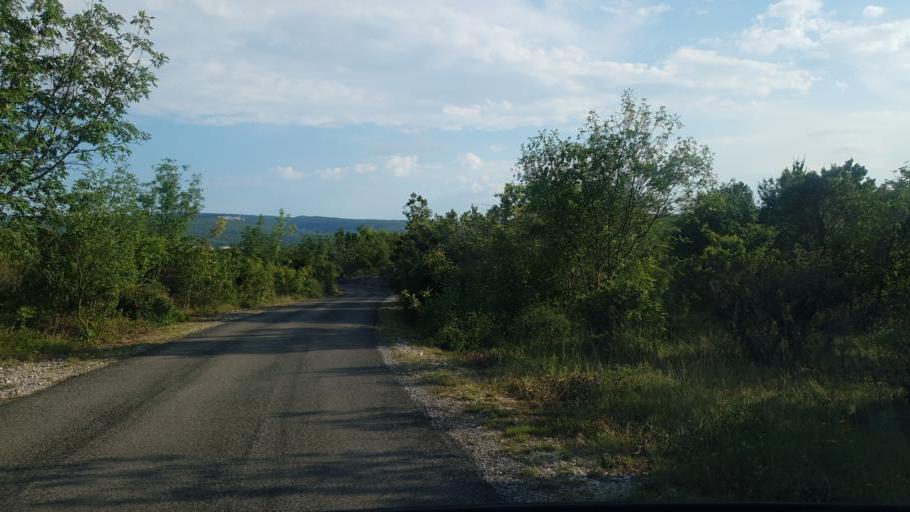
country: HR
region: Primorsko-Goranska
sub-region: Grad Crikvenica
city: Jadranovo
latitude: 45.1745
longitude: 14.6064
